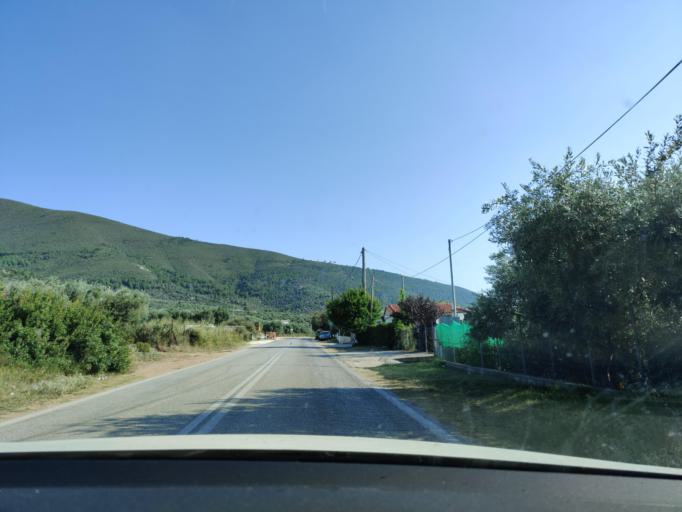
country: GR
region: East Macedonia and Thrace
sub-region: Nomos Kavalas
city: Prinos
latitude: 40.6892
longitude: 24.5266
